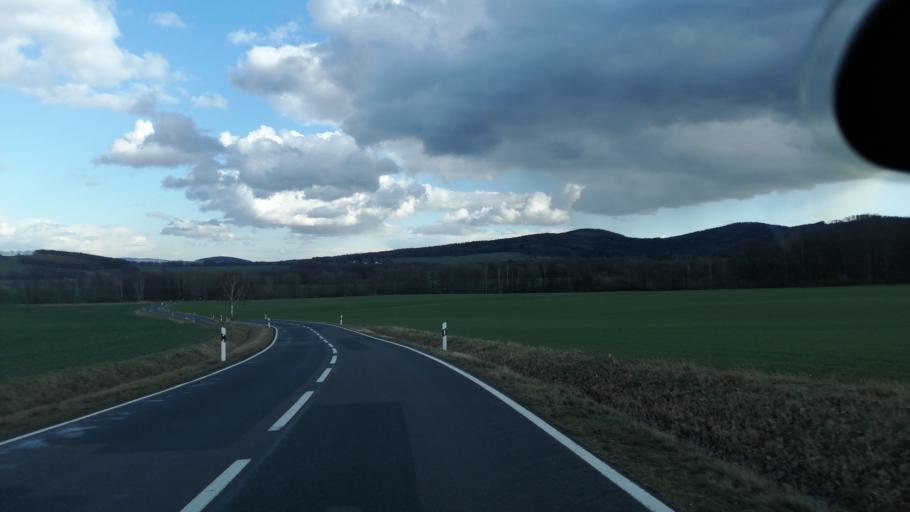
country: DE
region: Saxony
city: Cunewalde
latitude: 51.1366
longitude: 14.5233
